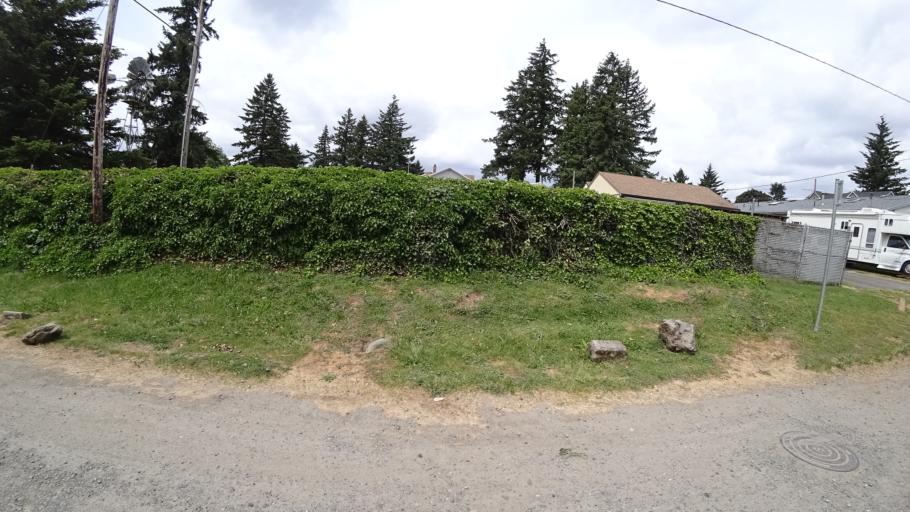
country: US
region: Oregon
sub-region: Multnomah County
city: Lents
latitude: 45.4681
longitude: -122.5739
